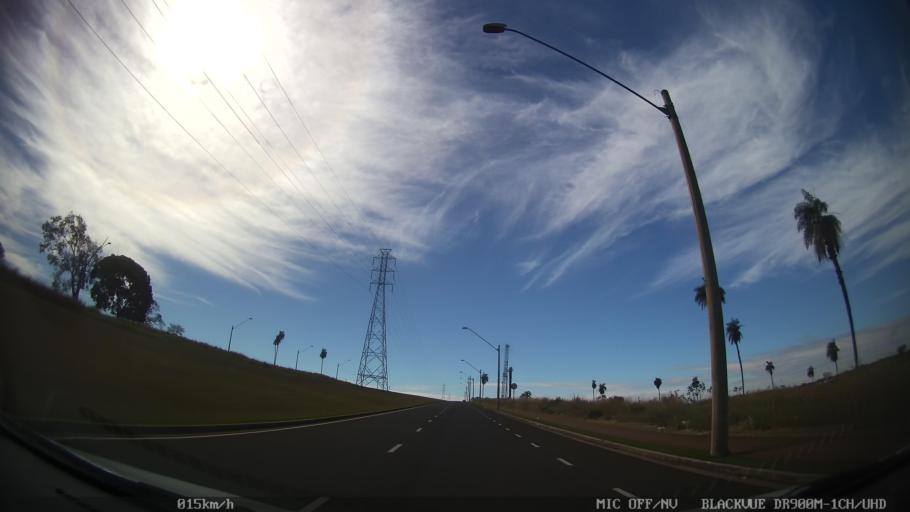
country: BR
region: Sao Paulo
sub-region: Sao Jose Do Rio Preto
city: Sao Jose do Rio Preto
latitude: -20.8586
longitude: -49.3799
